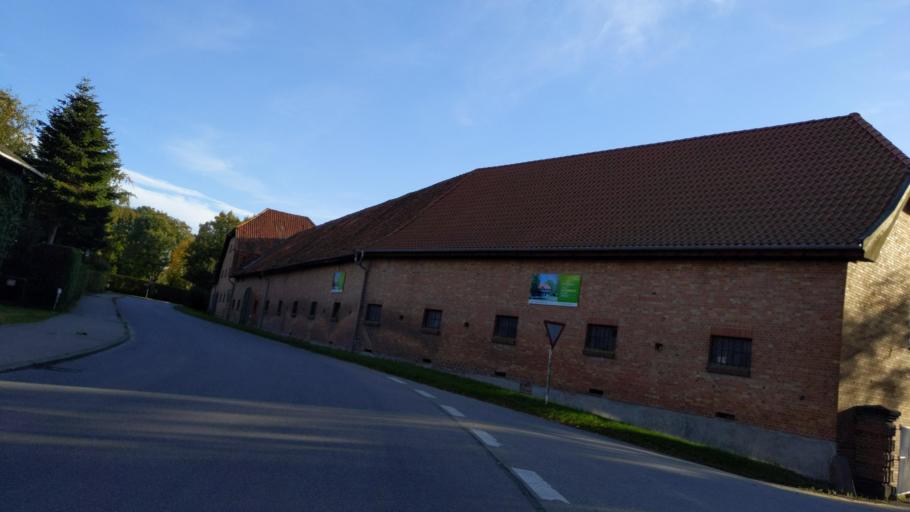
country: DE
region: Schleswig-Holstein
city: Ahrensbok
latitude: 54.0490
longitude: 10.5596
